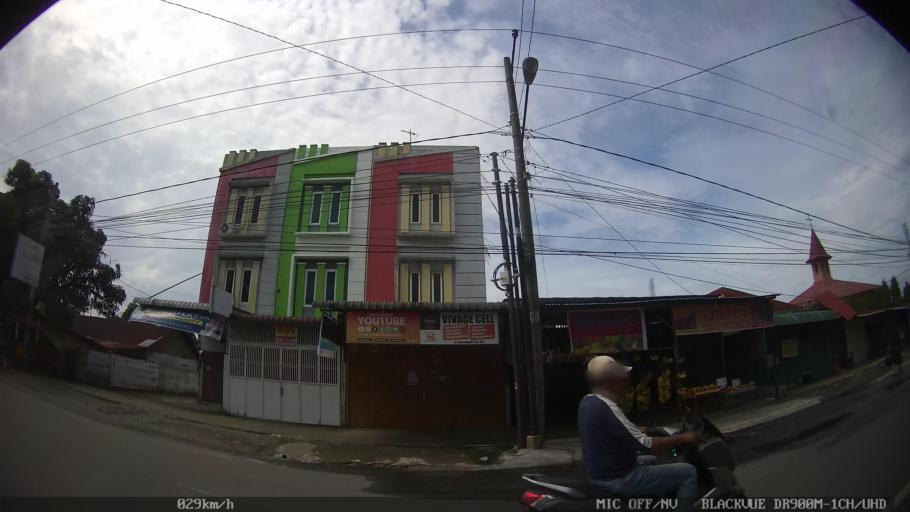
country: ID
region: North Sumatra
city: Medan
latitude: 3.6225
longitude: 98.6979
